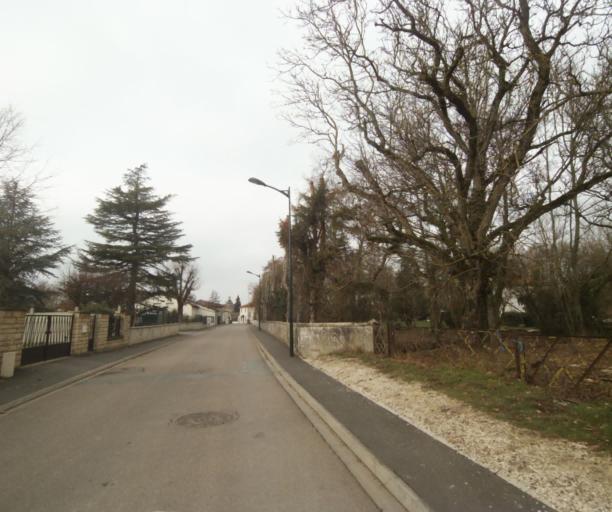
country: FR
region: Champagne-Ardenne
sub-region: Departement de la Haute-Marne
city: Villiers-en-Lieu
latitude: 48.6559
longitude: 4.8277
